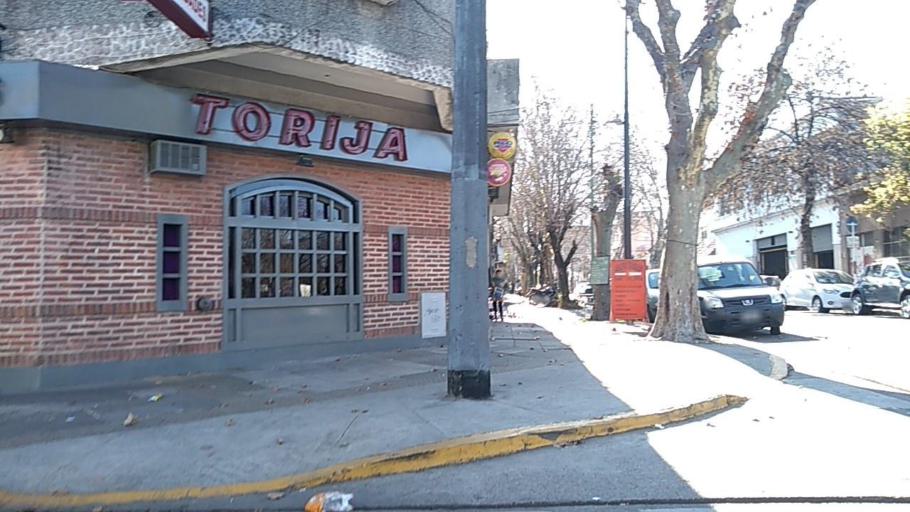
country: AR
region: Buenos Aires F.D.
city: Villa Santa Rita
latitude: -34.6209
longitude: -58.4914
